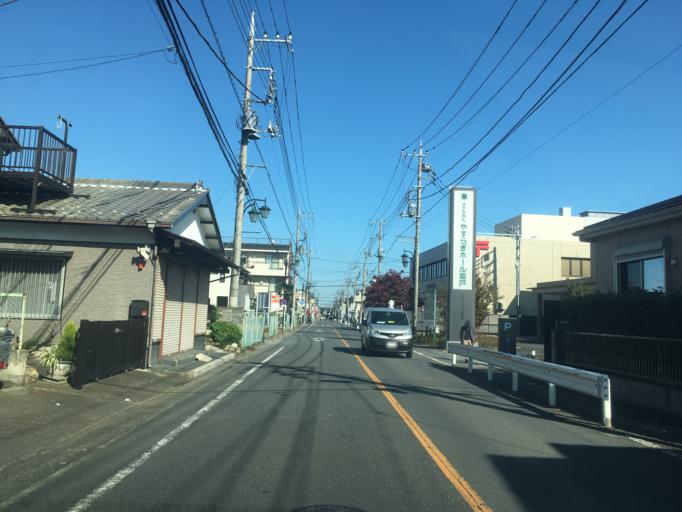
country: JP
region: Saitama
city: Sakado
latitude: 35.9589
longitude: 139.4044
